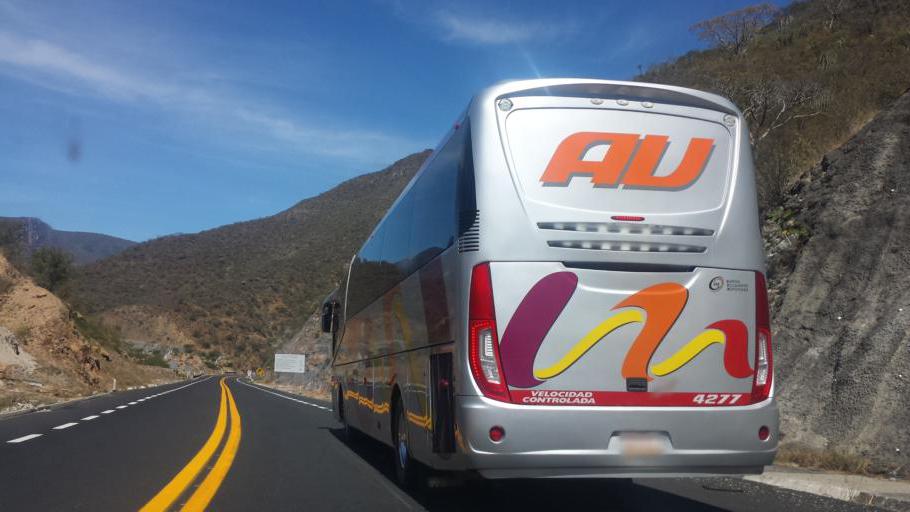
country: MX
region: Puebla
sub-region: San Jose Miahuatlan
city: San Pedro Tetitlan
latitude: 18.0974
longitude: -97.3367
